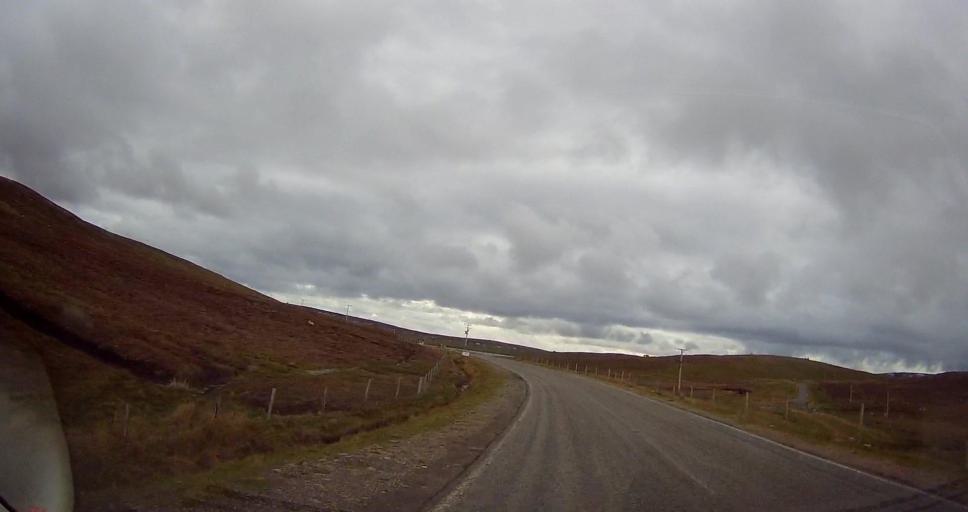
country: GB
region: Scotland
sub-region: Shetland Islands
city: Shetland
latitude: 60.6050
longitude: -1.0962
